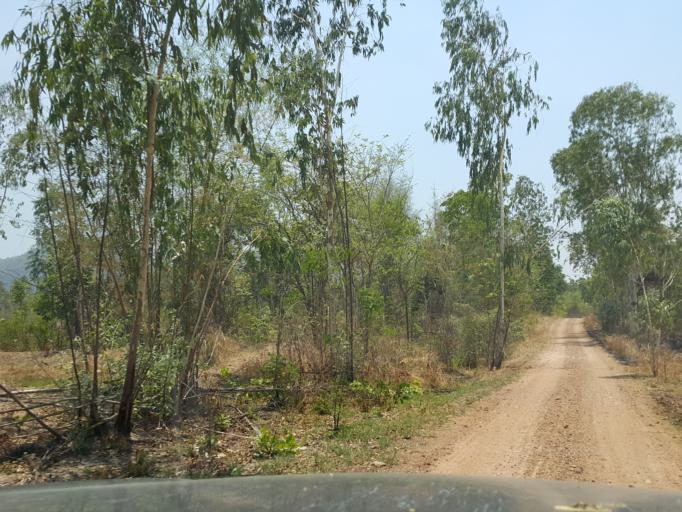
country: TH
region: Lampang
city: Thoen
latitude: 17.6401
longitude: 99.2768
